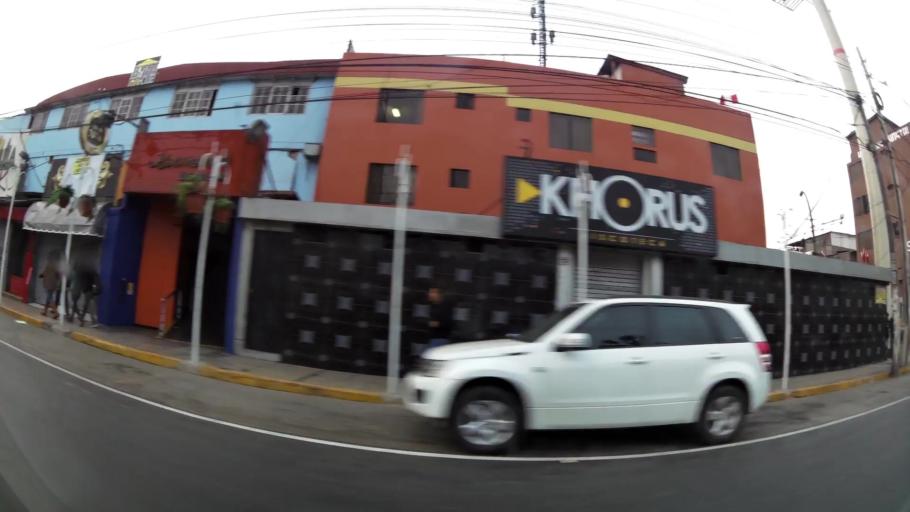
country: PE
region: Callao
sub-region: Callao
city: Callao
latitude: -12.0791
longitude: -77.0777
